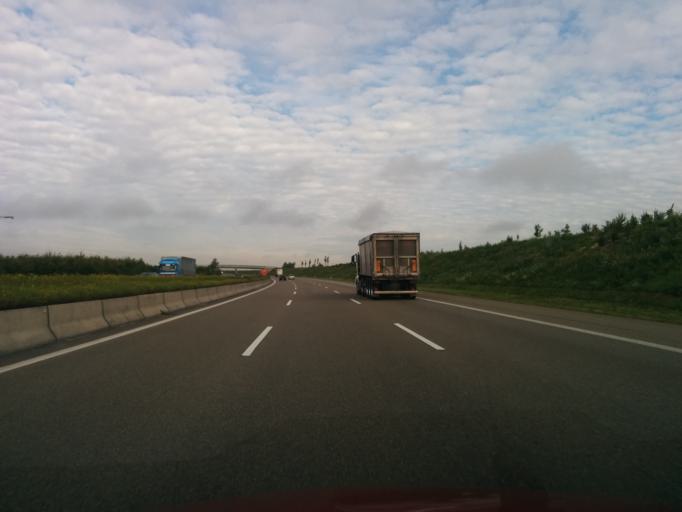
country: DE
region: Bavaria
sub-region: Swabia
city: Leipheim
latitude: 48.4546
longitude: 10.1971
